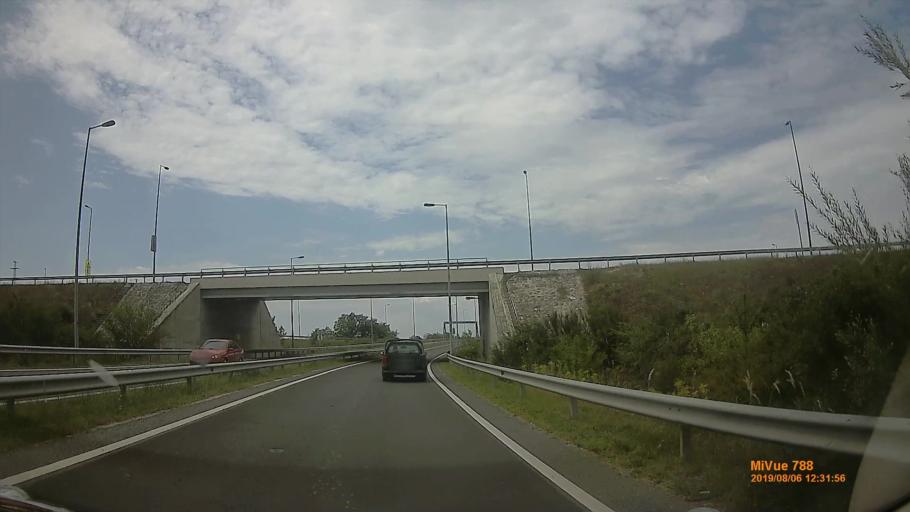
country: HU
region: Vas
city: Szombathely
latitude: 47.2478
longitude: 16.6553
